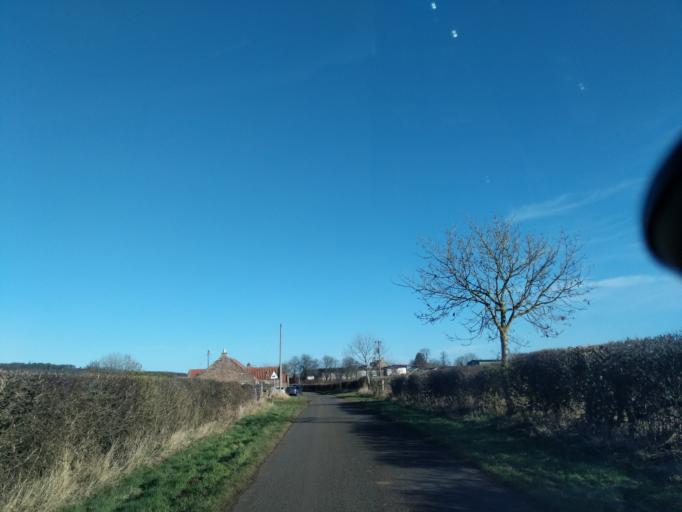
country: GB
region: Scotland
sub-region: East Lothian
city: East Linton
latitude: 55.9666
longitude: -2.6996
